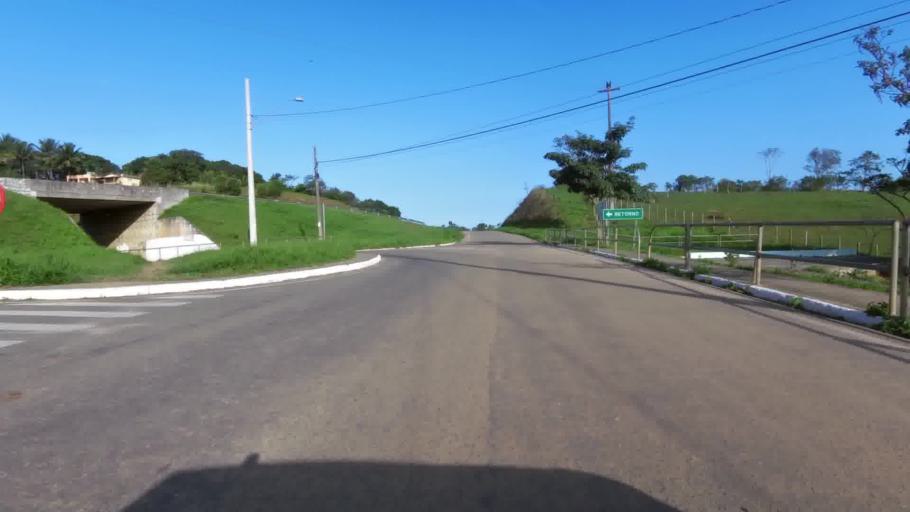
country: BR
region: Espirito Santo
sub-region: Guarapari
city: Guarapari
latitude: -20.7309
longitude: -40.5591
